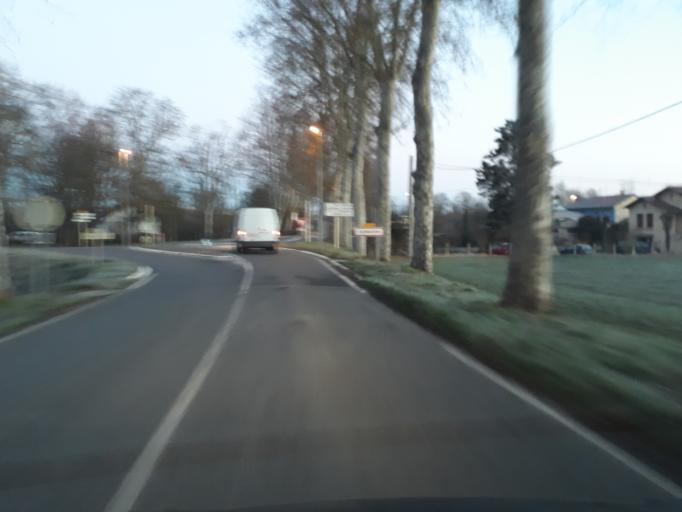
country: FR
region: Midi-Pyrenees
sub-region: Departement du Gers
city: Samatan
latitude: 43.4861
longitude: 0.9349
